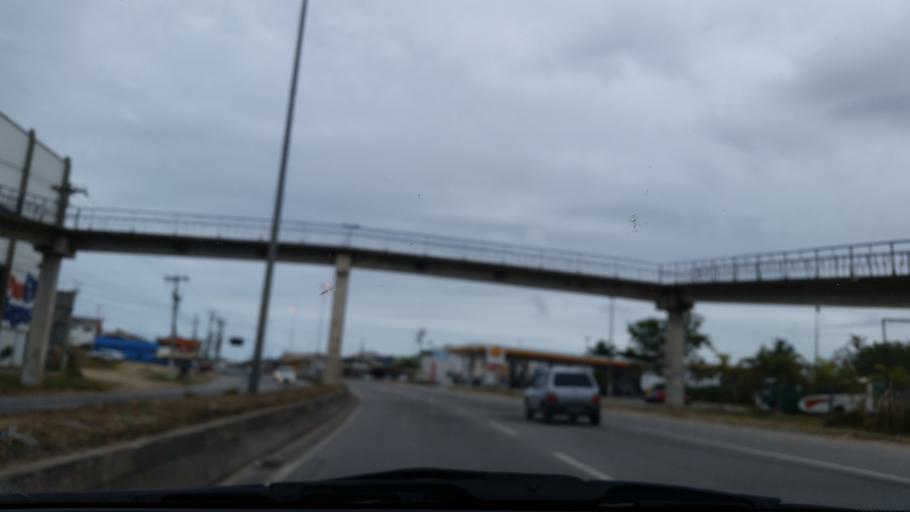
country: BR
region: Rio de Janeiro
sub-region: Sao Pedro Da Aldeia
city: Sao Pedro da Aldeia
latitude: -22.8322
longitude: -42.1324
